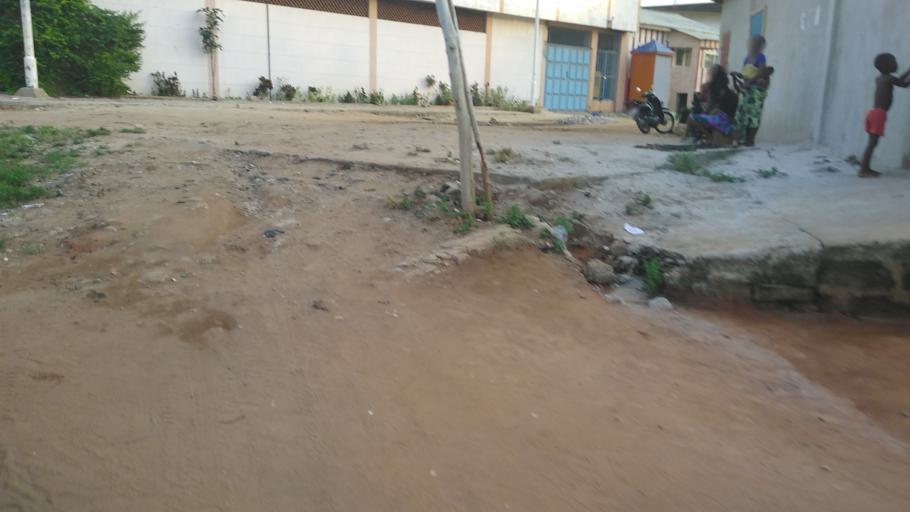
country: BJ
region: Atlantique
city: Abomey-Calavi
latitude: 6.4082
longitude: 2.3399
